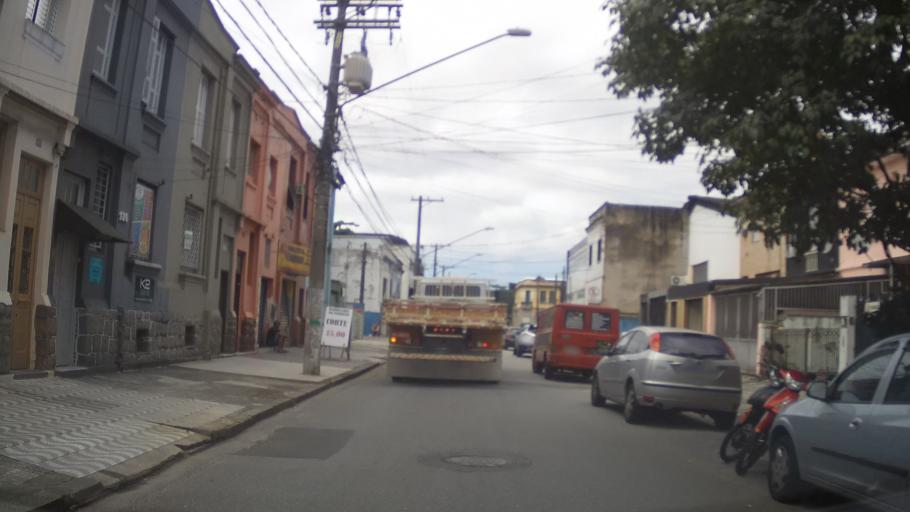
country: BR
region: Sao Paulo
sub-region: Santos
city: Santos
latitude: -23.9550
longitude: -46.3183
